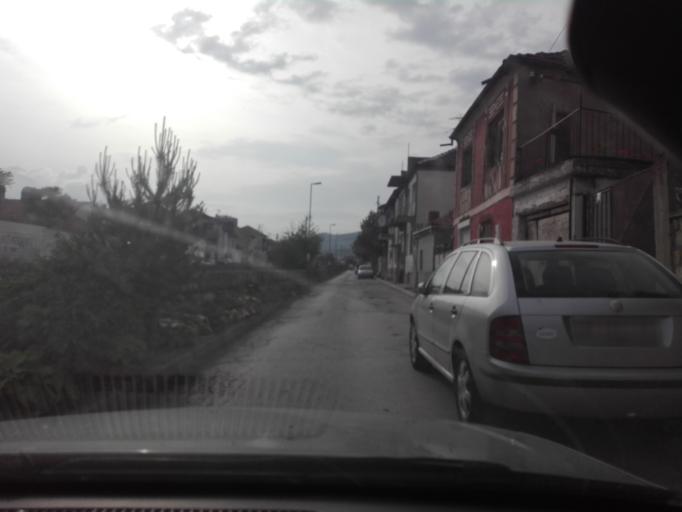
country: MK
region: Bitola
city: Bitola
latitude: 41.0301
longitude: 21.3453
